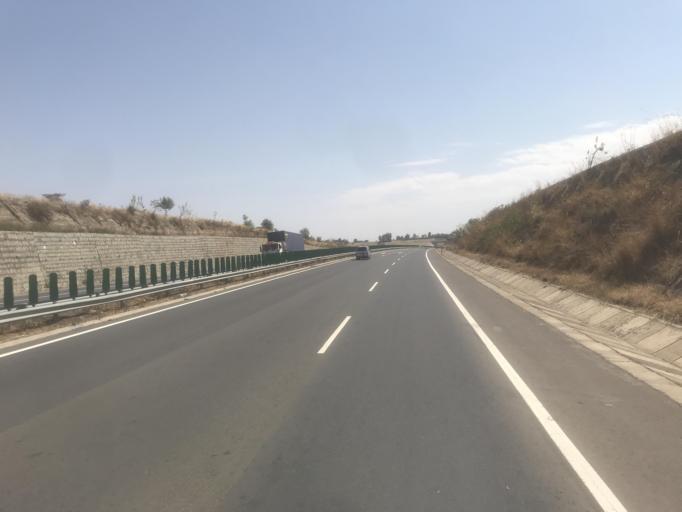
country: ET
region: Oromiya
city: Mojo
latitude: 8.5834
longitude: 39.1677
